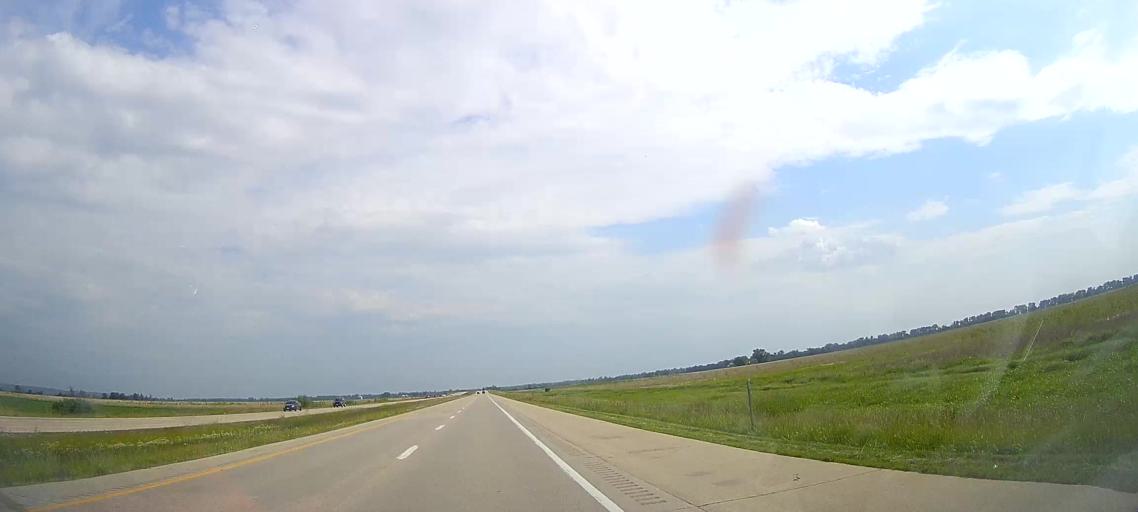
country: US
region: Nebraska
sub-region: Burt County
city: Tekamah
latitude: 41.8740
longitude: -96.1040
